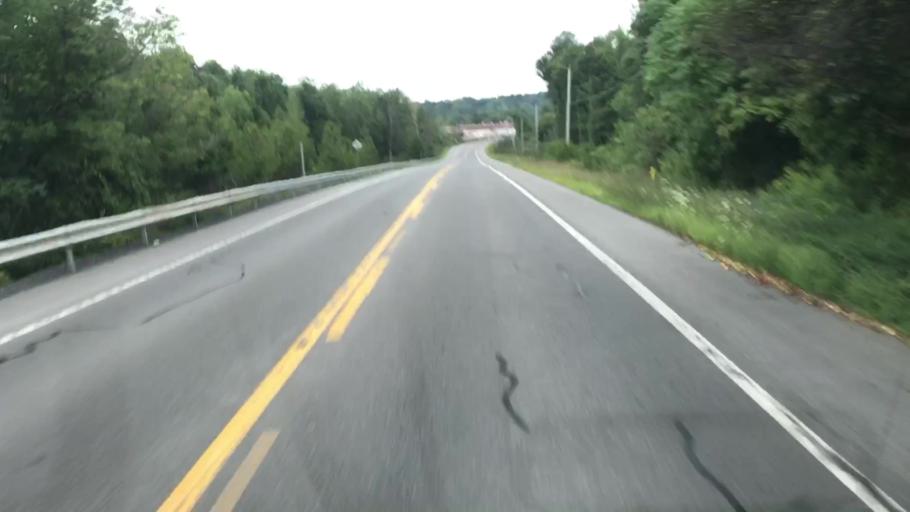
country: US
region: New York
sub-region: Onondaga County
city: Camillus
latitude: 43.0527
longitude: -76.3112
